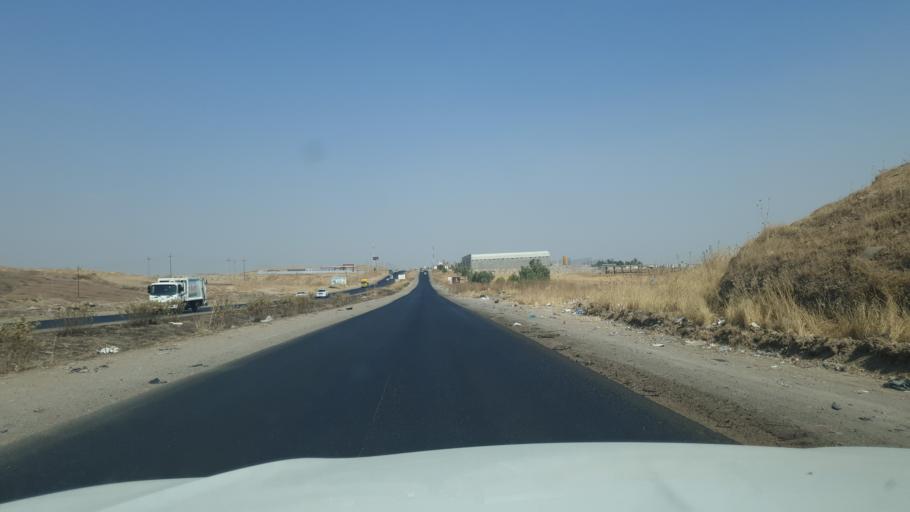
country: IQ
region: Arbil
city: Erbil
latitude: 36.1976
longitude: 43.8888
